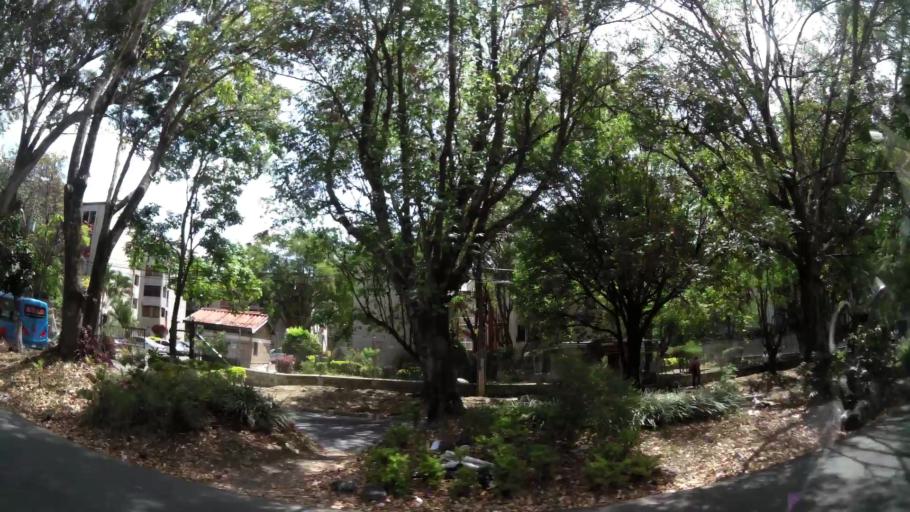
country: CO
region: Antioquia
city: Bello
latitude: 6.3408
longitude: -75.5484
